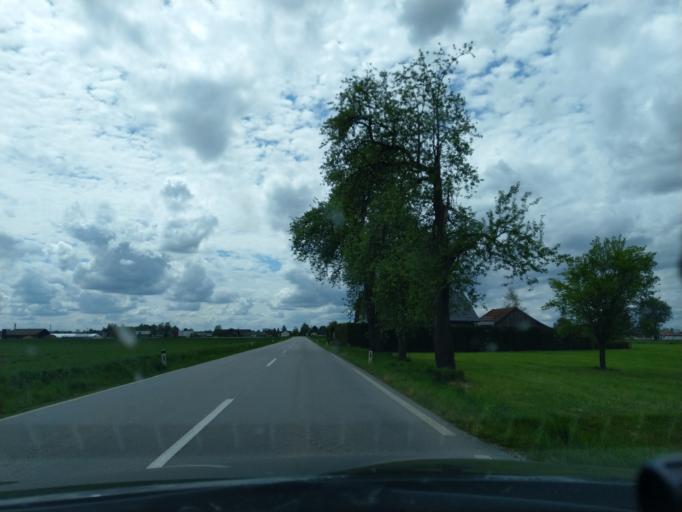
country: DE
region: Bavaria
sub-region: Lower Bavaria
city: Bad Fussing
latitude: 48.3398
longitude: 13.3719
